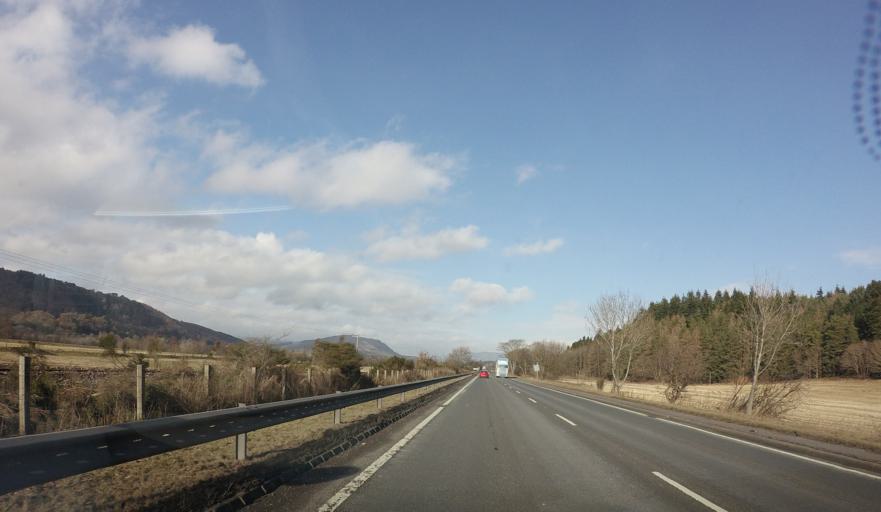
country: GB
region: Scotland
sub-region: Perth and Kinross
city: Pitlochry
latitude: 56.6252
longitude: -3.6372
